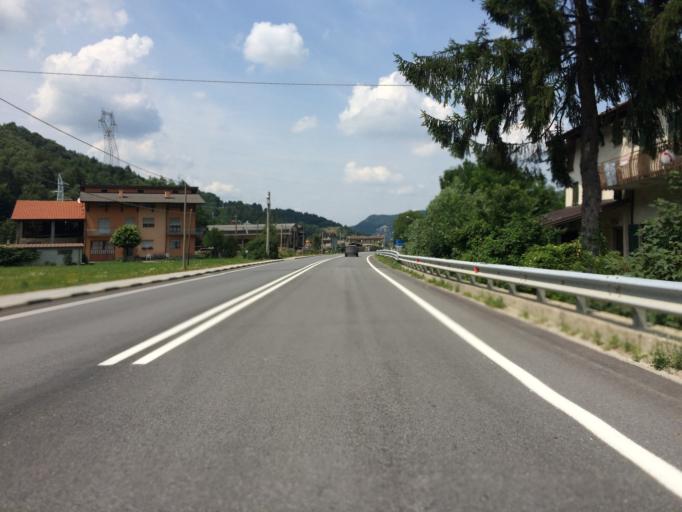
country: IT
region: Piedmont
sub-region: Provincia di Cuneo
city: Robilante
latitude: 44.2763
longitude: 7.5183
